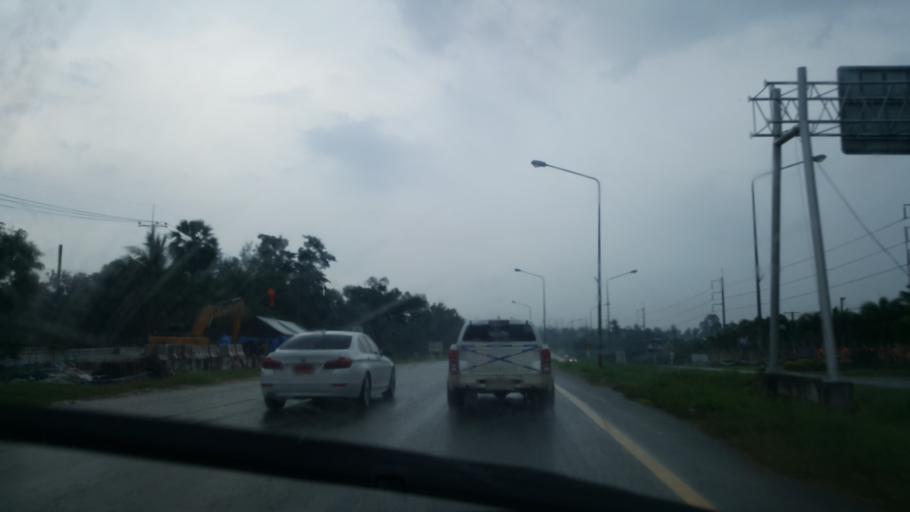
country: TH
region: Chon Buri
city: Ban Talat Bueng
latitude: 12.9513
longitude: 101.0468
